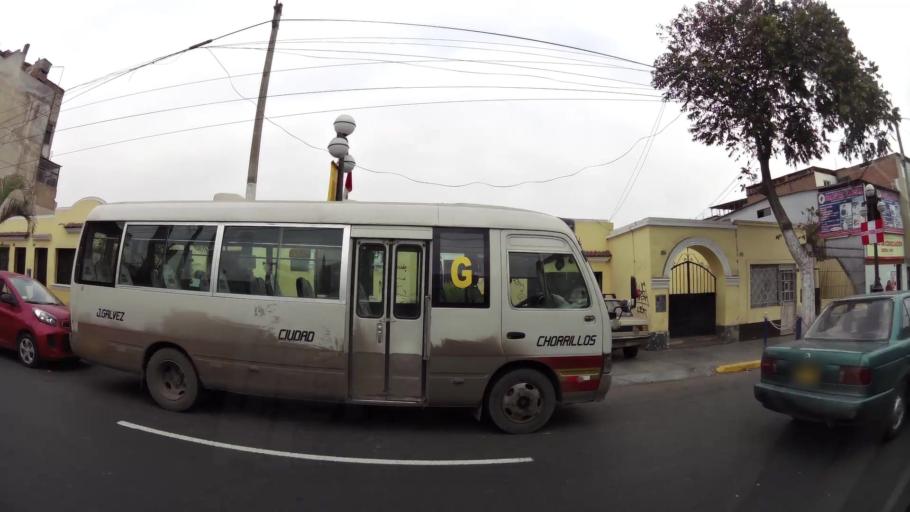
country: PE
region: Lima
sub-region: Lima
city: Surco
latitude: -12.1677
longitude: -77.0264
